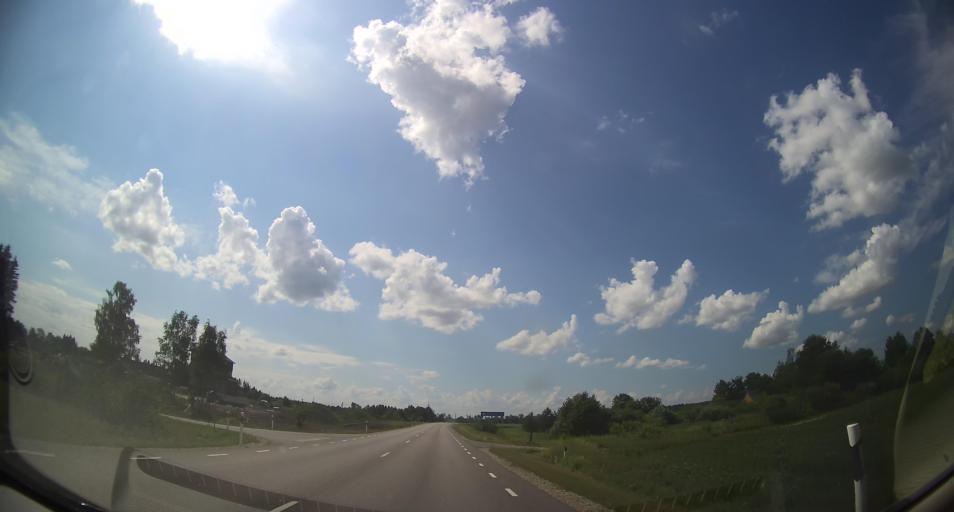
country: EE
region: Raplamaa
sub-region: Maerjamaa vald
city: Marjamaa
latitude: 58.9166
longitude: 24.2916
